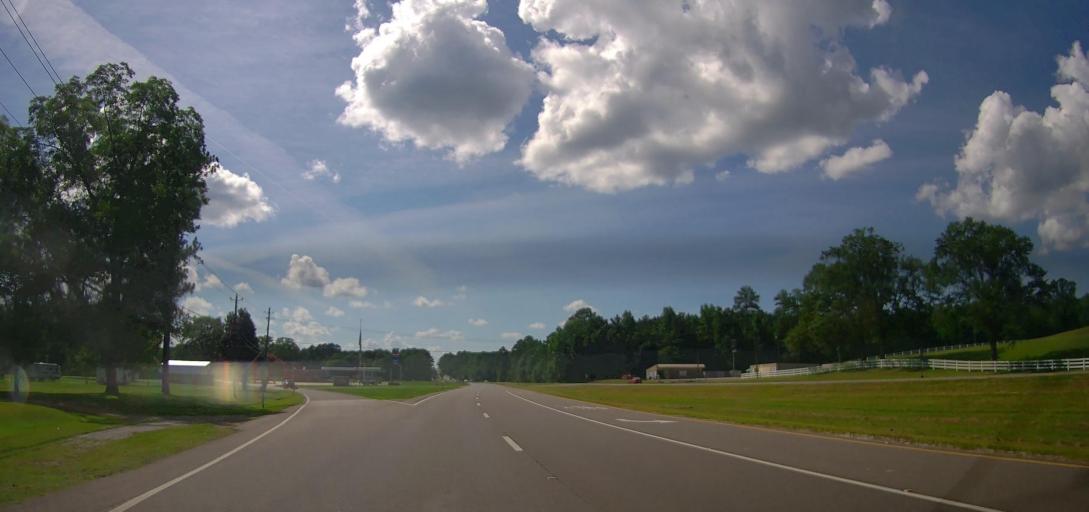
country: US
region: Alabama
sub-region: Tuscaloosa County
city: Northport
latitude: 33.2446
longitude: -87.6715
